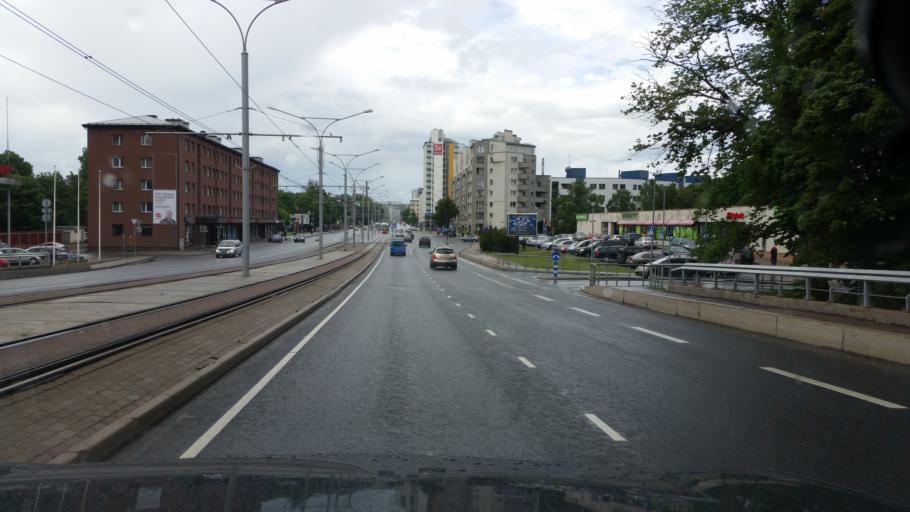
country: EE
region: Harju
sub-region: Tallinna linn
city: Tallinn
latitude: 59.4176
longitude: 24.7407
